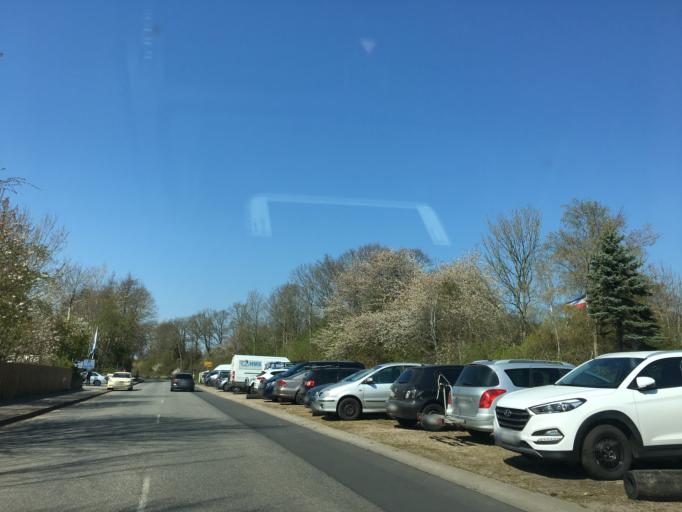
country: DE
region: Schleswig-Holstein
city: Dollrottfeld
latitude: 54.5861
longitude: 9.8172
